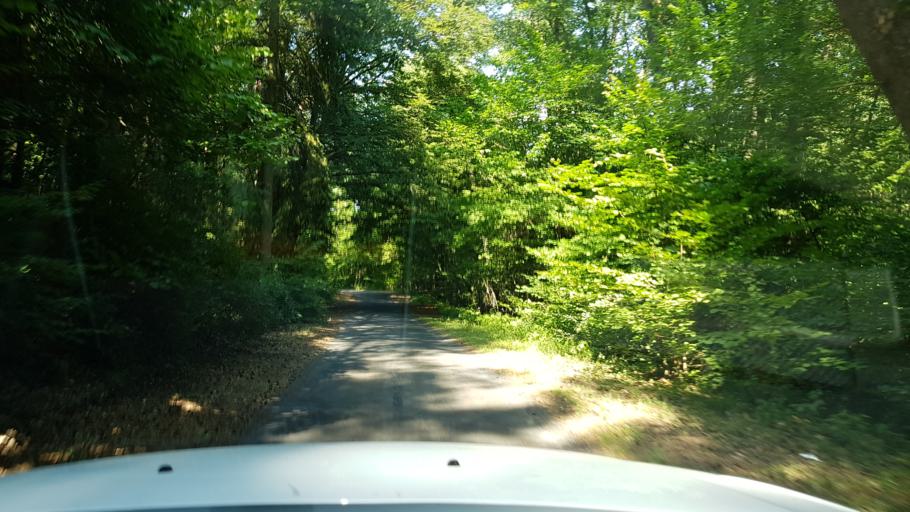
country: PL
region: West Pomeranian Voivodeship
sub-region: Powiat gryfinski
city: Moryn
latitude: 52.8082
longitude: 14.3178
